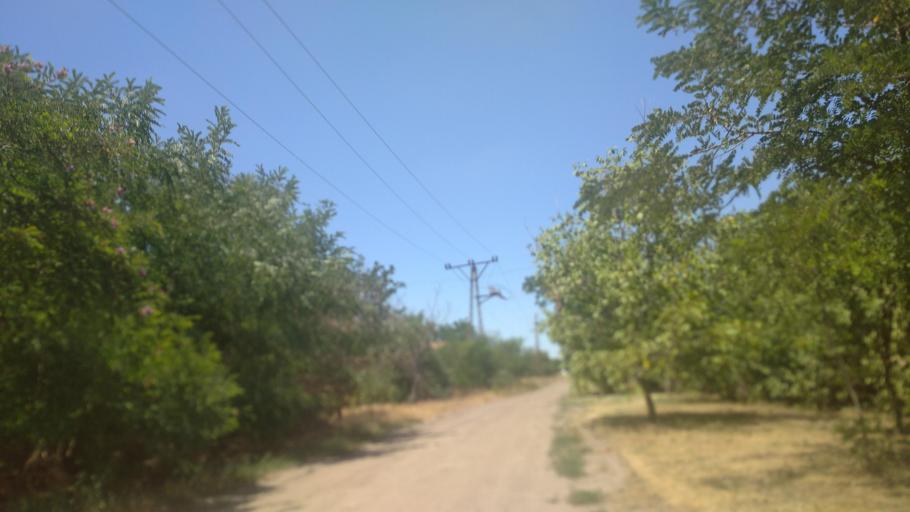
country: HU
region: Bekes
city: Oroshaza
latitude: 46.5560
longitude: 20.6223
